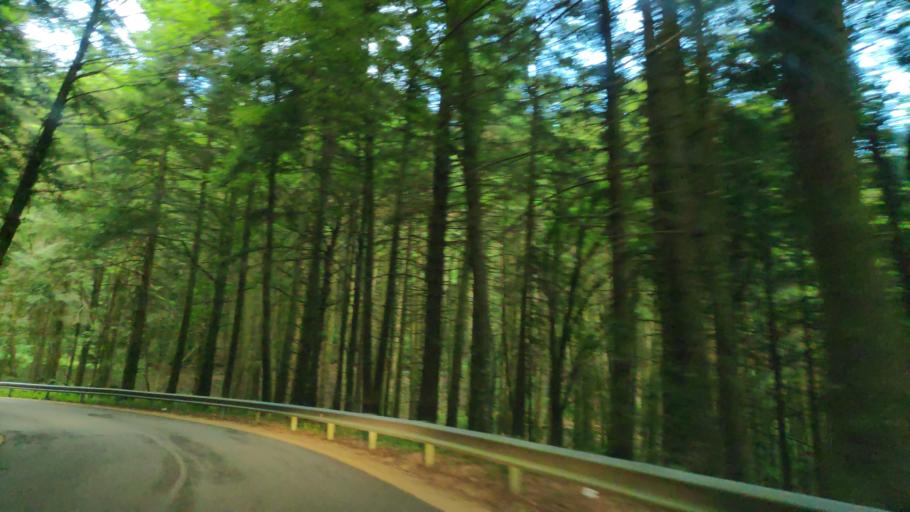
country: IT
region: Calabria
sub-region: Provincia di Vibo-Valentia
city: Mongiana
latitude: 38.5362
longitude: 16.3322
